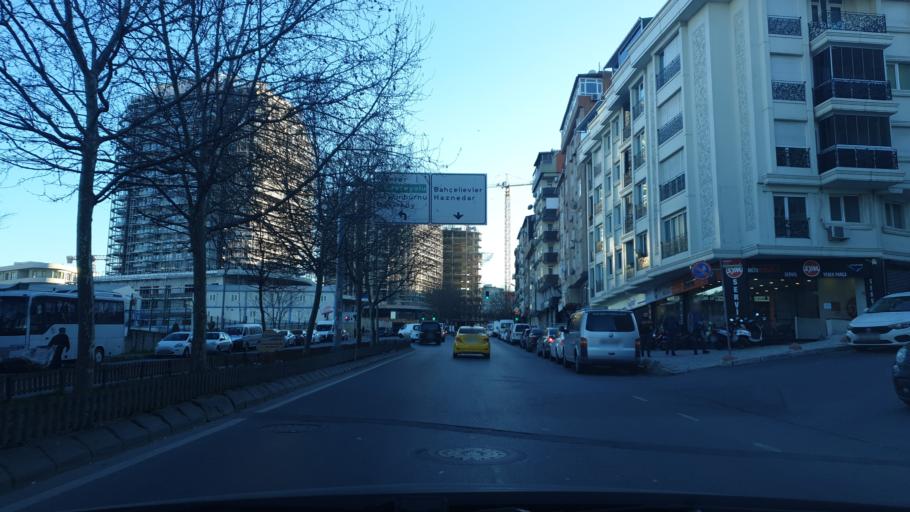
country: TR
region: Istanbul
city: merter keresteciler
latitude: 41.0134
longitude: 28.8780
